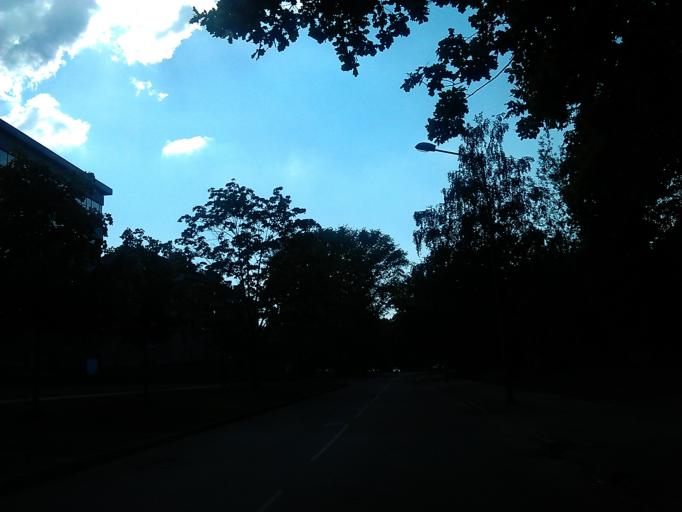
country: LV
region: Riga
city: Jaunciems
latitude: 56.9835
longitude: 24.1579
